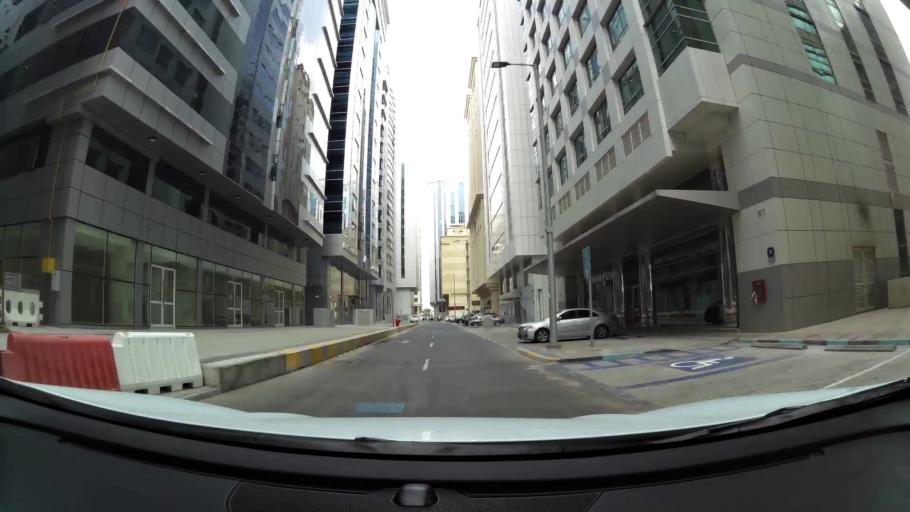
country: AE
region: Abu Dhabi
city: Abu Dhabi
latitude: 24.4662
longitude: 54.3856
